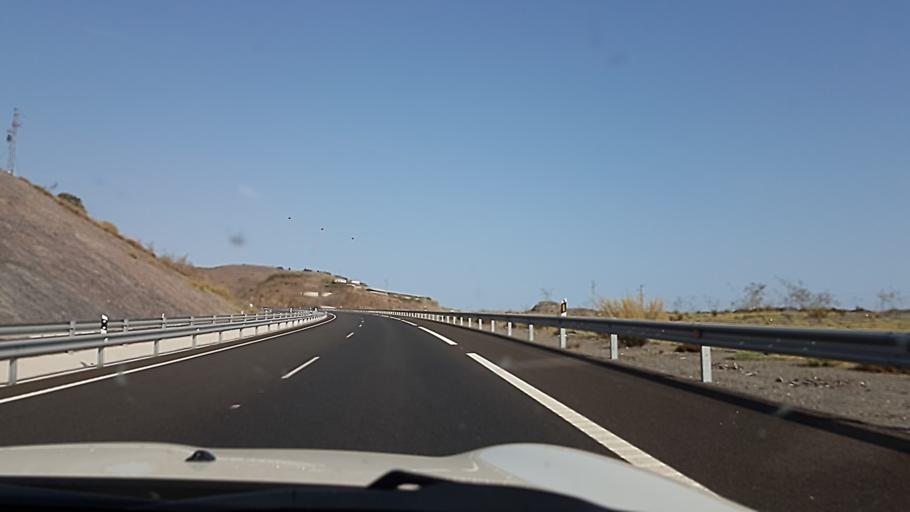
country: ES
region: Andalusia
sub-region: Provincia de Granada
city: Albunol
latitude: 36.7562
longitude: -3.2331
